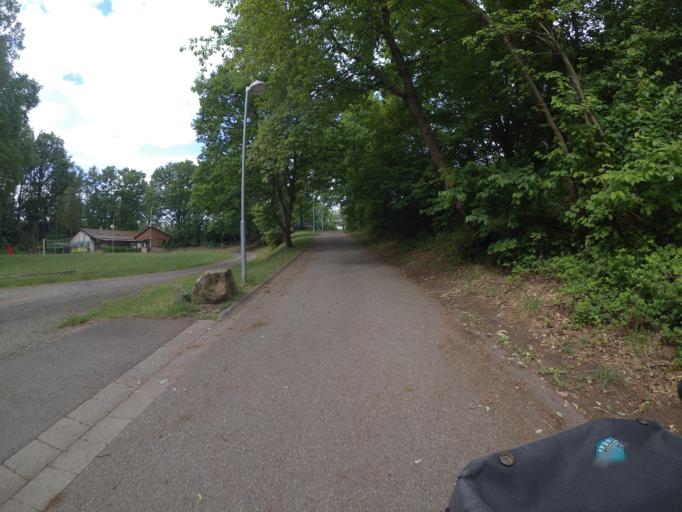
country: DE
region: Rheinland-Pfalz
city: Weilerbach
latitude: 49.4821
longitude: 7.6443
